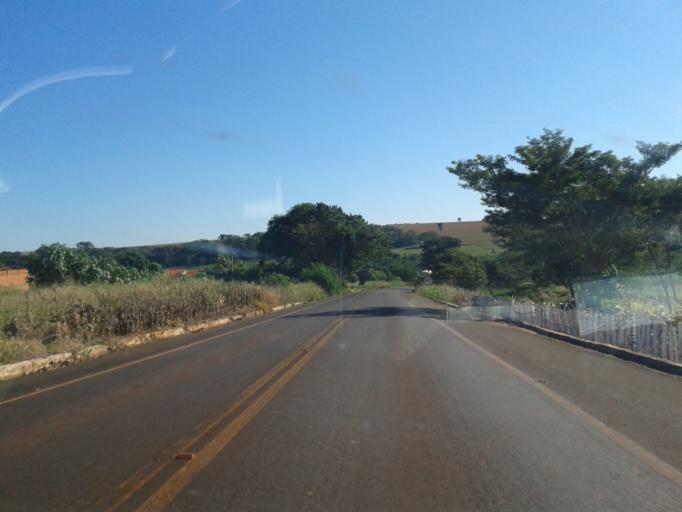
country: BR
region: Minas Gerais
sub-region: Capinopolis
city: Capinopolis
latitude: -18.6813
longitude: -49.5644
